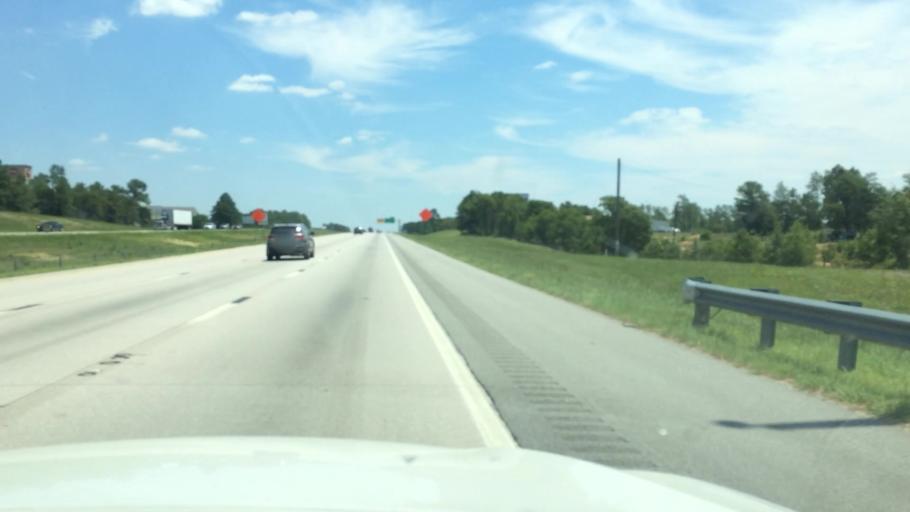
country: US
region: South Carolina
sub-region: Kershaw County
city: Elgin
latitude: 34.1012
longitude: -80.8385
